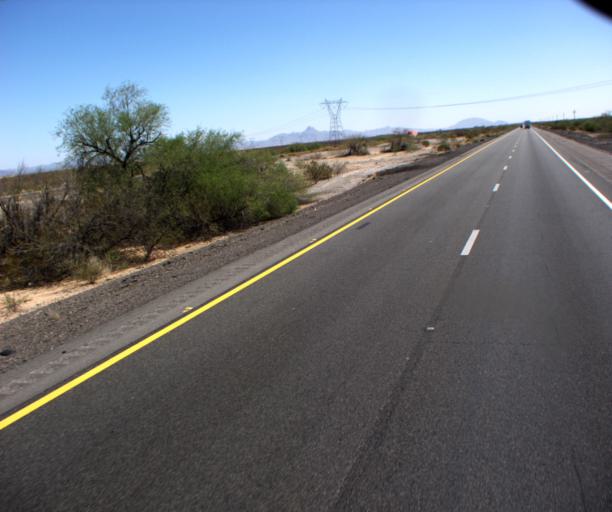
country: US
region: Arizona
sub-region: La Paz County
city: Salome
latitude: 33.5761
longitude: -113.4022
